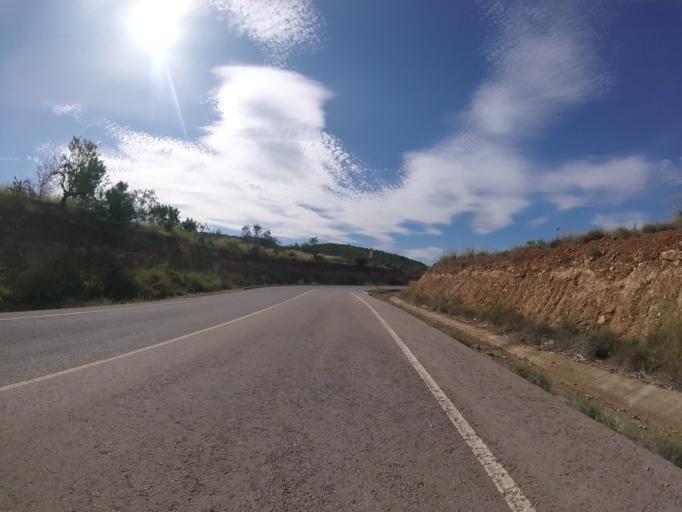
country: ES
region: Valencia
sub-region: Provincia de Castello
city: Peniscola
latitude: 40.3942
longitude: 0.3589
